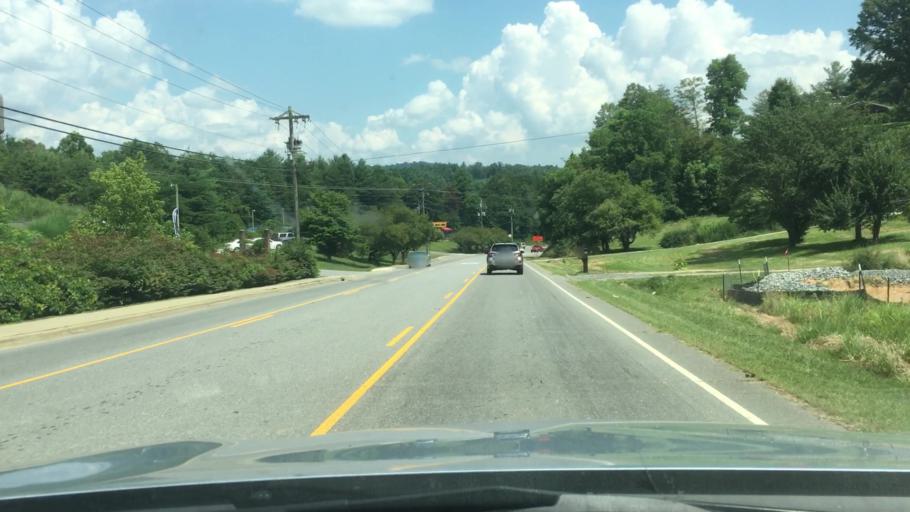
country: US
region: North Carolina
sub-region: Madison County
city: Mars Hill
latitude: 35.8213
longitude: -82.5405
